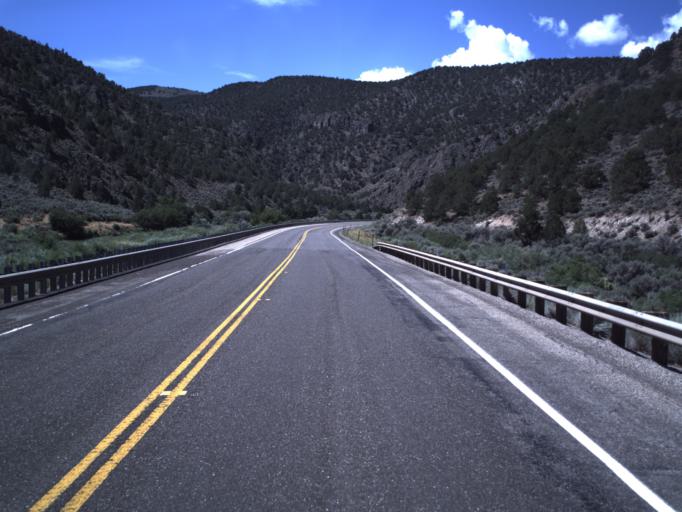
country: US
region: Utah
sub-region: Piute County
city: Junction
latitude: 38.1235
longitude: -112.3321
